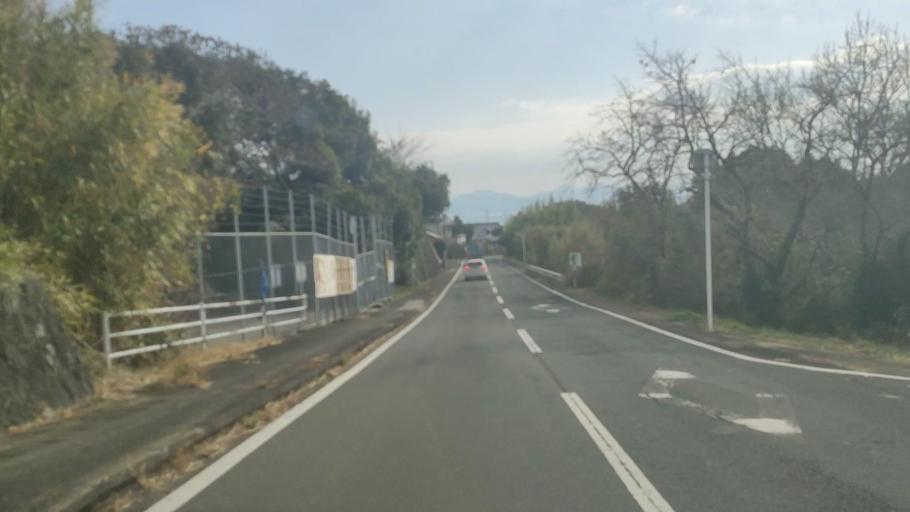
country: JP
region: Nagasaki
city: Shimabara
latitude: 32.6754
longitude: 130.2814
